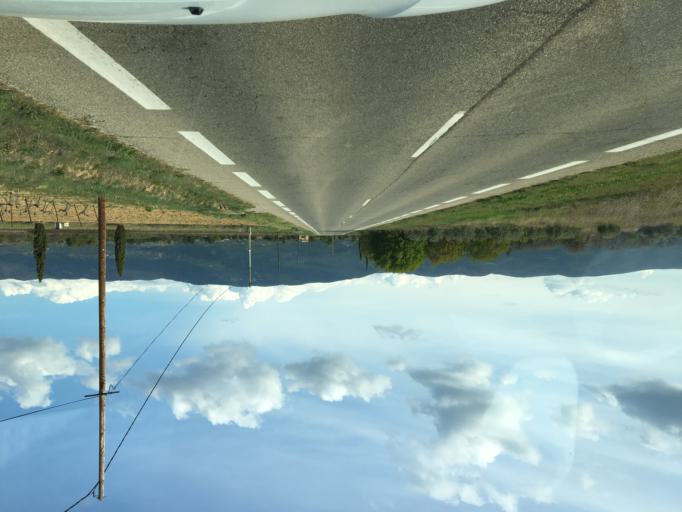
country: FR
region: Provence-Alpes-Cote d'Azur
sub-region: Departement du Vaucluse
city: Ansouis
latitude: 43.7484
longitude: 5.4621
